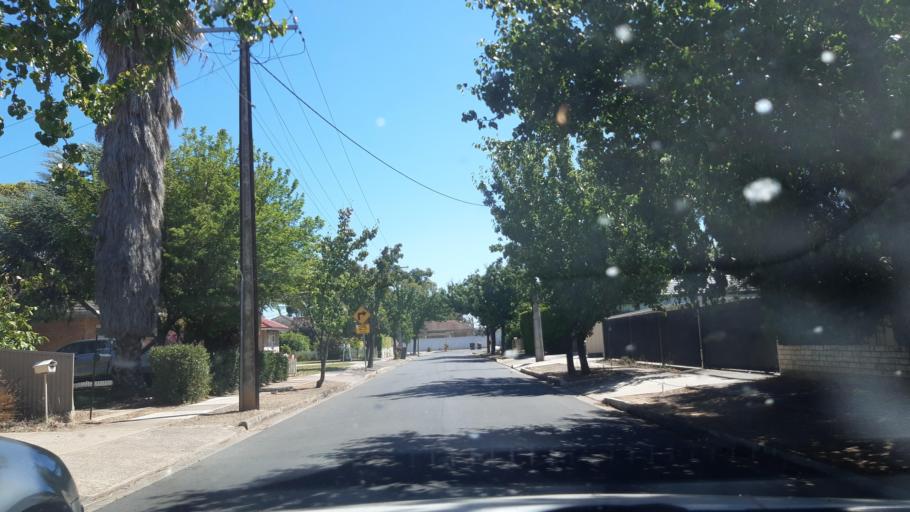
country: AU
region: South Australia
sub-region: Marion
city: Clovelly Park
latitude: -34.9899
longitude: 138.5663
